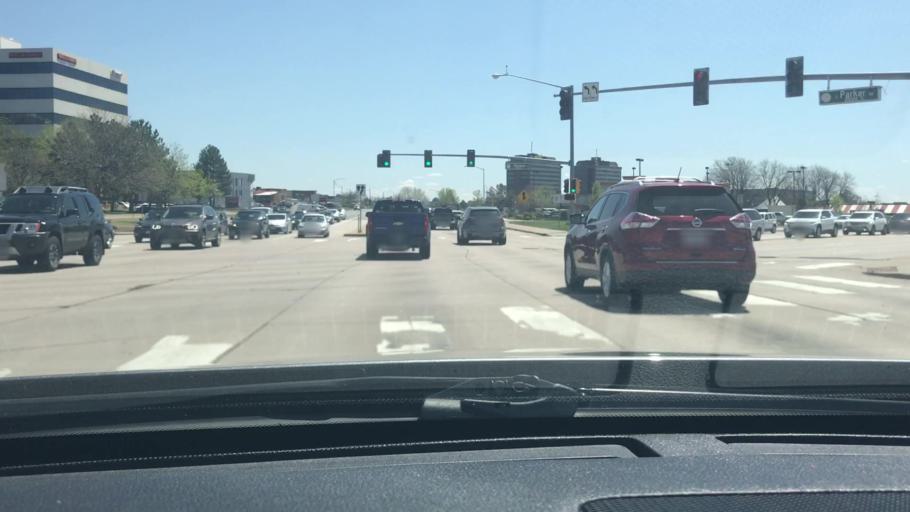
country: US
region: Colorado
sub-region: Adams County
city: Aurora
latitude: 39.6710
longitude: -104.8663
